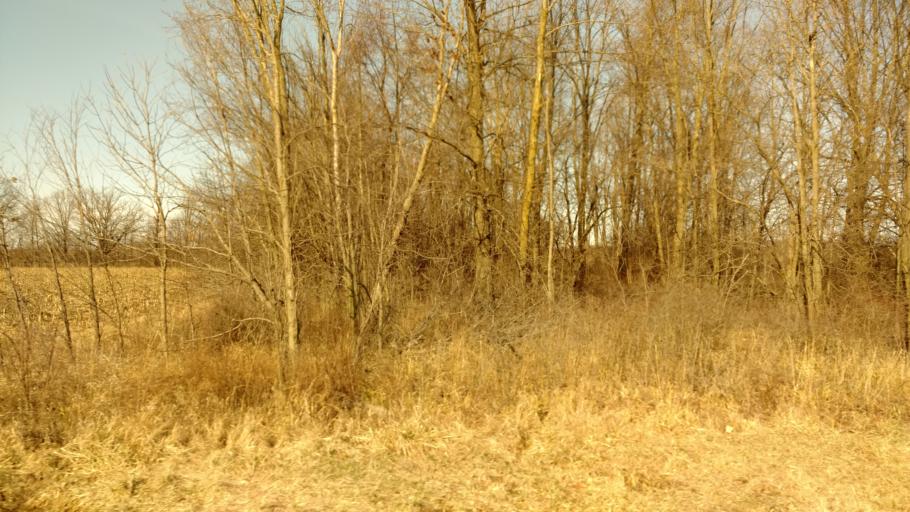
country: US
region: Ohio
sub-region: Wyandot County
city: Upper Sandusky
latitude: 40.6945
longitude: -83.3766
